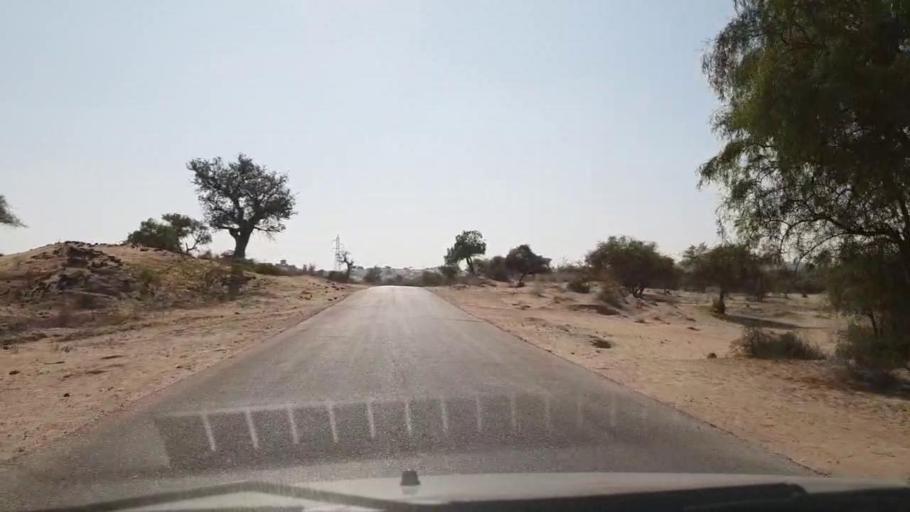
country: PK
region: Sindh
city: Mithi
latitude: 24.5986
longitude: 69.7145
